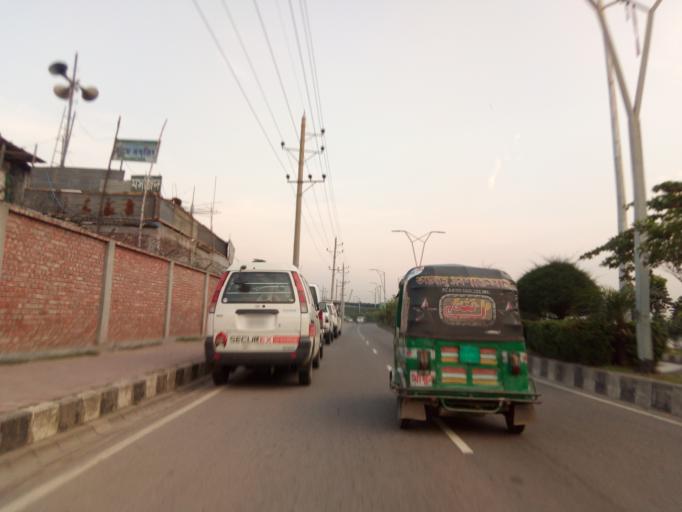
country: BD
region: Dhaka
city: Paltan
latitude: 23.7627
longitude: 90.4114
